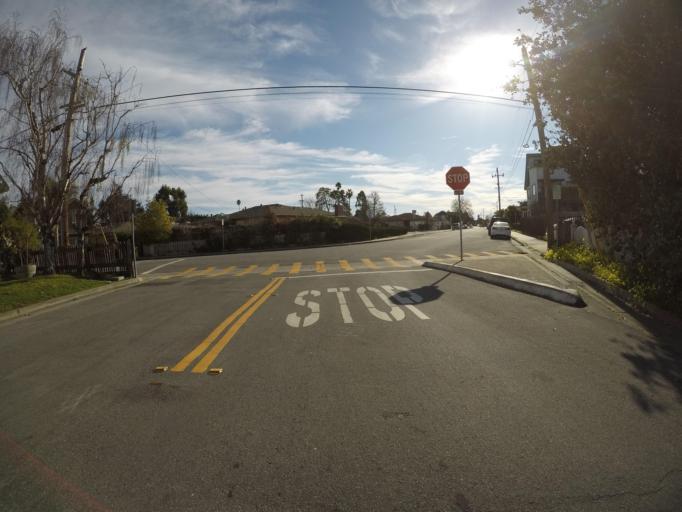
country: US
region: California
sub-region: Santa Cruz County
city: Santa Cruz
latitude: 36.9664
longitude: -122.0375
